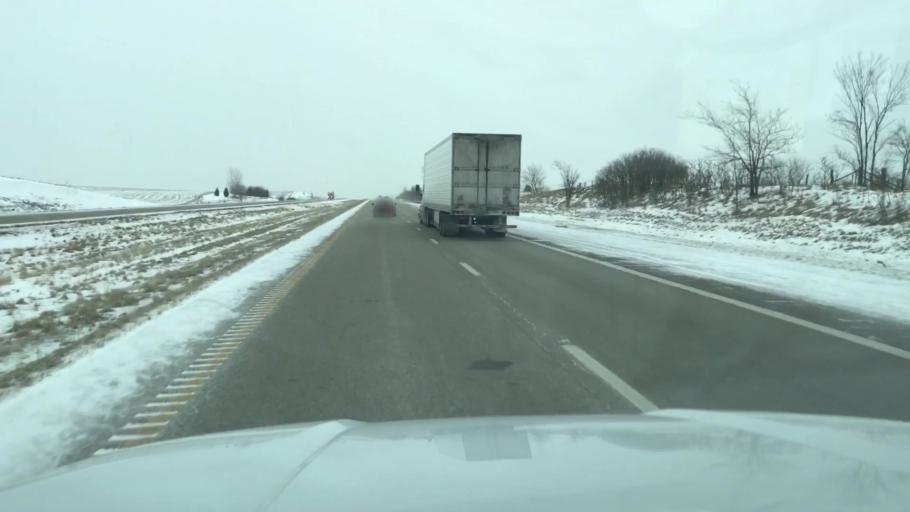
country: US
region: Missouri
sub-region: Andrew County
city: Country Club Village
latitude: 39.7476
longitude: -94.6933
